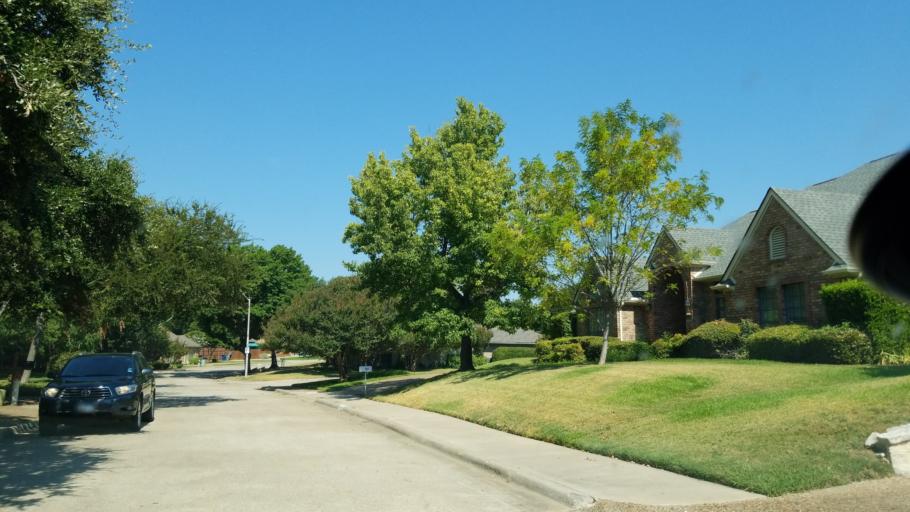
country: US
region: Texas
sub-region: Dallas County
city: Richardson
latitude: 32.9101
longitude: -96.7143
